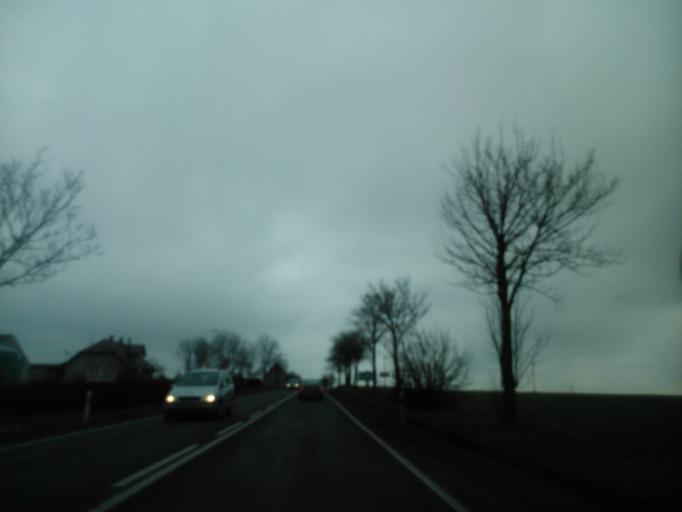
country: PL
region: Kujawsko-Pomorskie
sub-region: Powiat torunski
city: Lubicz Gorny
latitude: 53.0859
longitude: 18.7709
